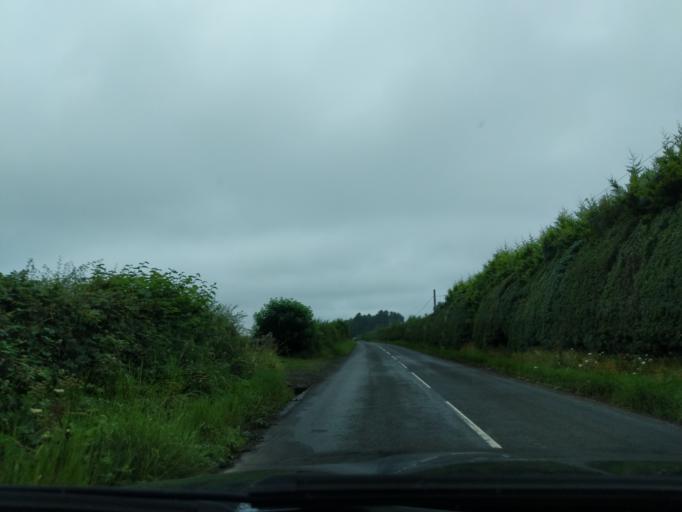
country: GB
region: England
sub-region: Northumberland
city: Lowick
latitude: 55.6488
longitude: -2.0022
